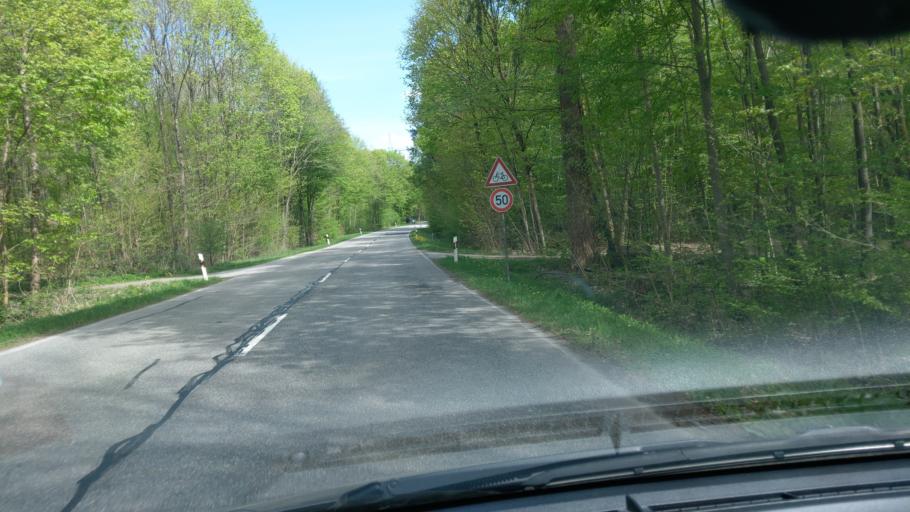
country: DE
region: Saarland
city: Spiesen-Elversberg
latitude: 49.2969
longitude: 7.1322
